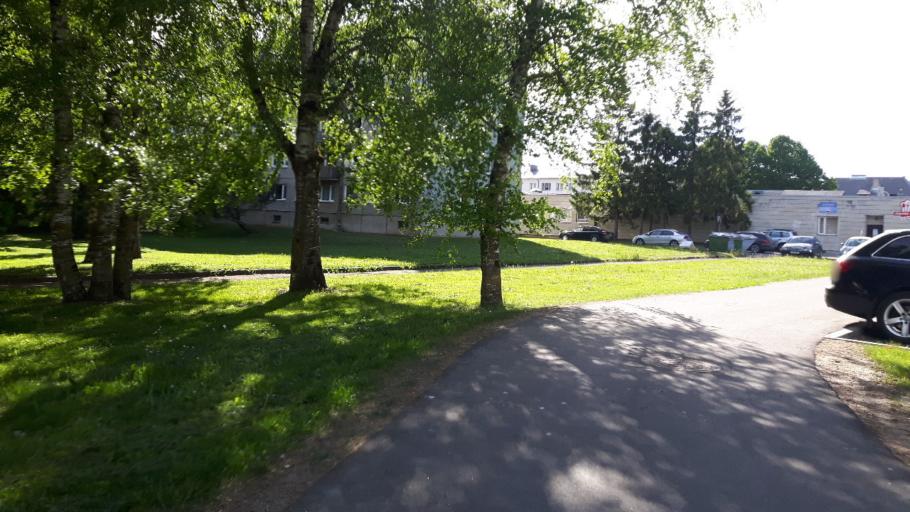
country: EE
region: Harju
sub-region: Joelaehtme vald
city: Loo
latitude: 59.4337
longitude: 24.9482
